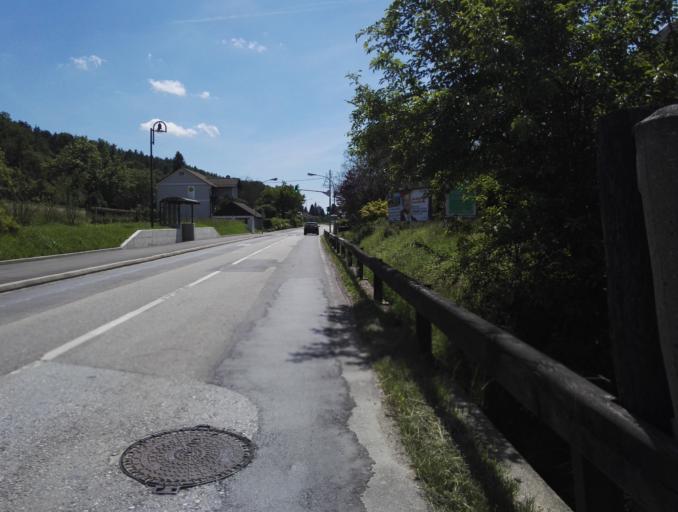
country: AT
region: Styria
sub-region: Politischer Bezirk Graz-Umgebung
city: Grambach
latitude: 47.0115
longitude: 15.5026
